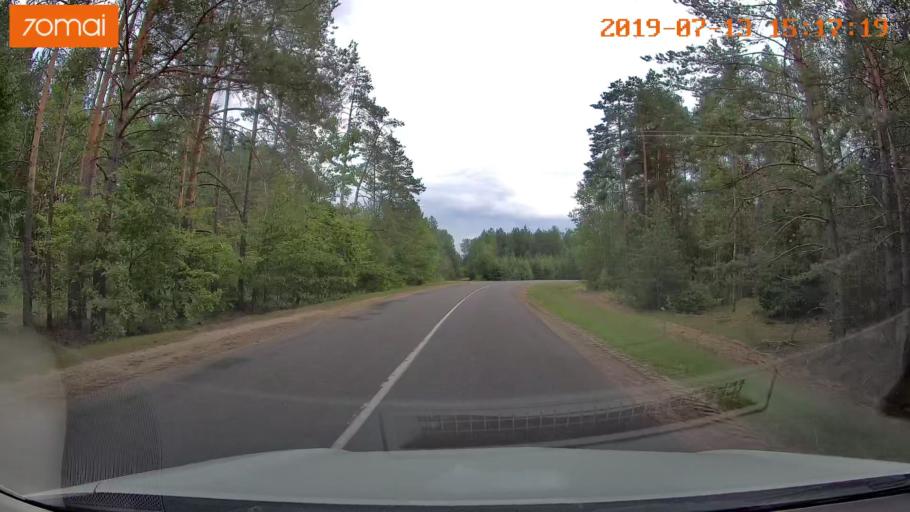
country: BY
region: Mogilev
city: Hlusha
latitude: 53.0972
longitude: 28.8432
